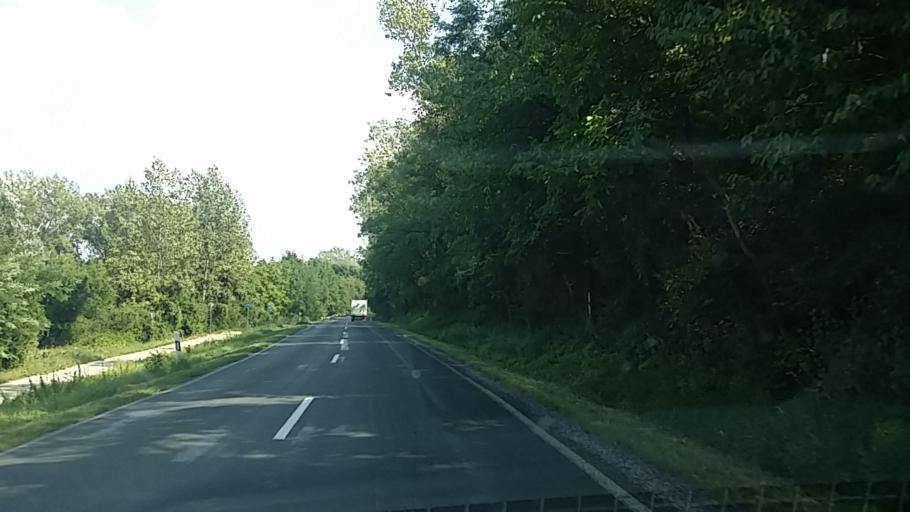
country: HU
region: Gyor-Moson-Sopron
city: Nagycenk
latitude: 47.6306
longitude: 16.7311
